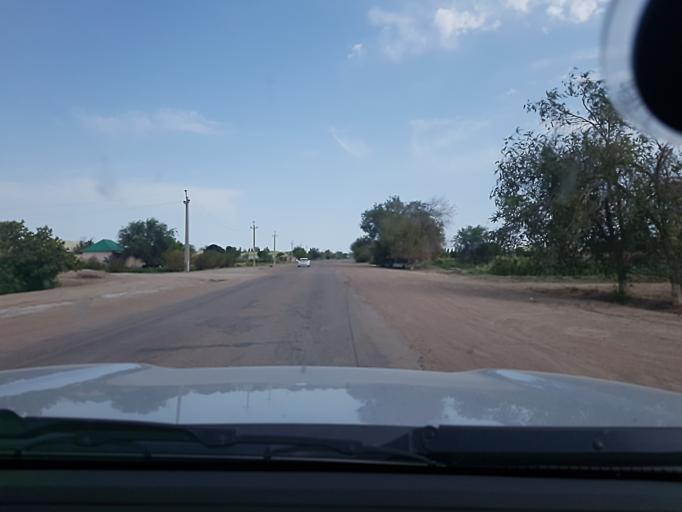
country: TM
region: Dasoguz
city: Boldumsaz
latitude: 42.0193
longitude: 59.8419
